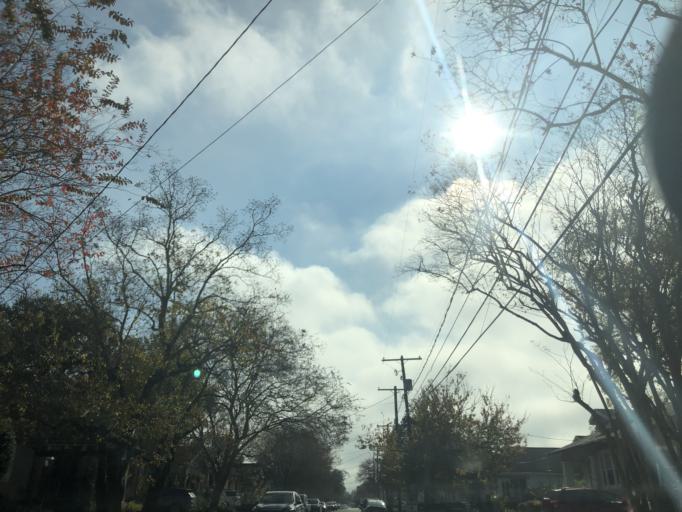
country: US
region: Louisiana
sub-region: Jefferson Parish
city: Metairie
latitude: 29.9816
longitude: -90.1528
